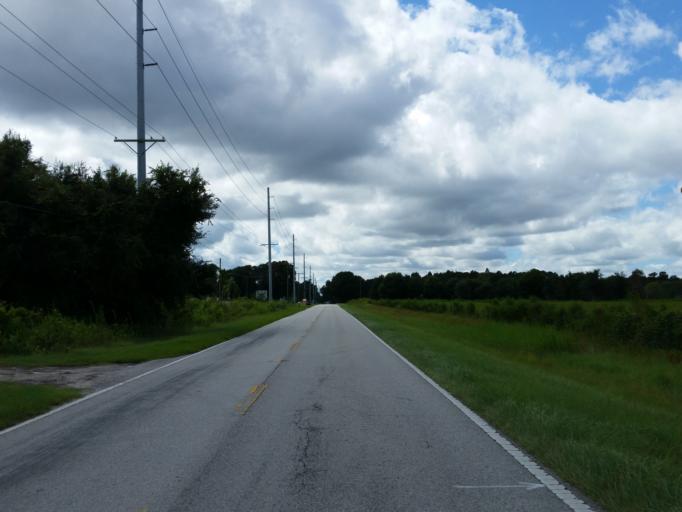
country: US
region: Florida
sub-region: Pasco County
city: Zephyrhills West
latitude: 28.1704
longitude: -82.2612
